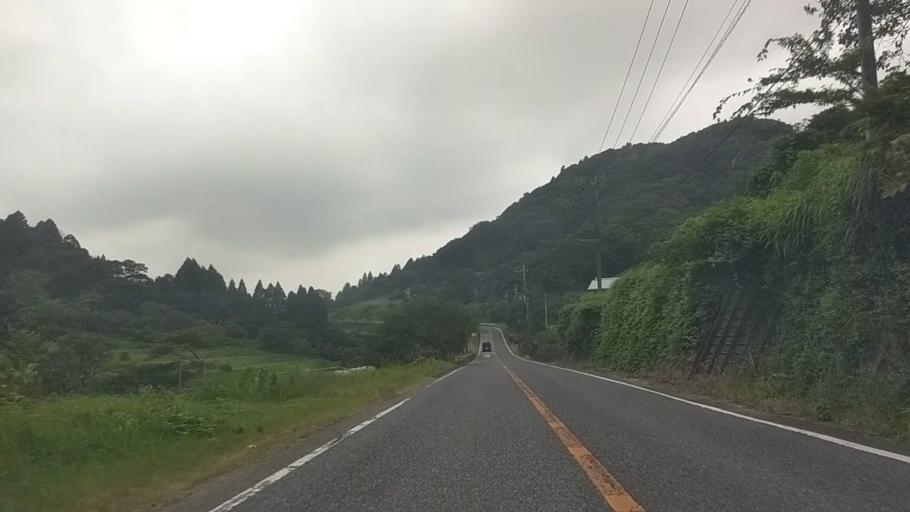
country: JP
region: Chiba
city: Tateyama
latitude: 35.1439
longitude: 139.9246
